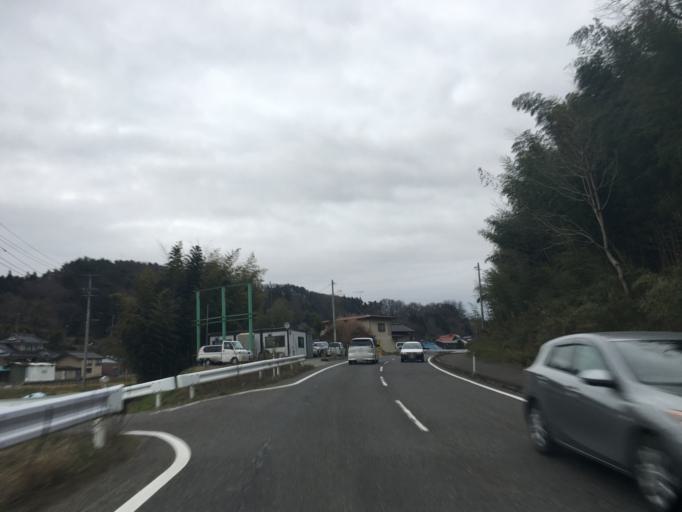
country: JP
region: Fukushima
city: Koriyama
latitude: 37.3921
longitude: 140.4307
